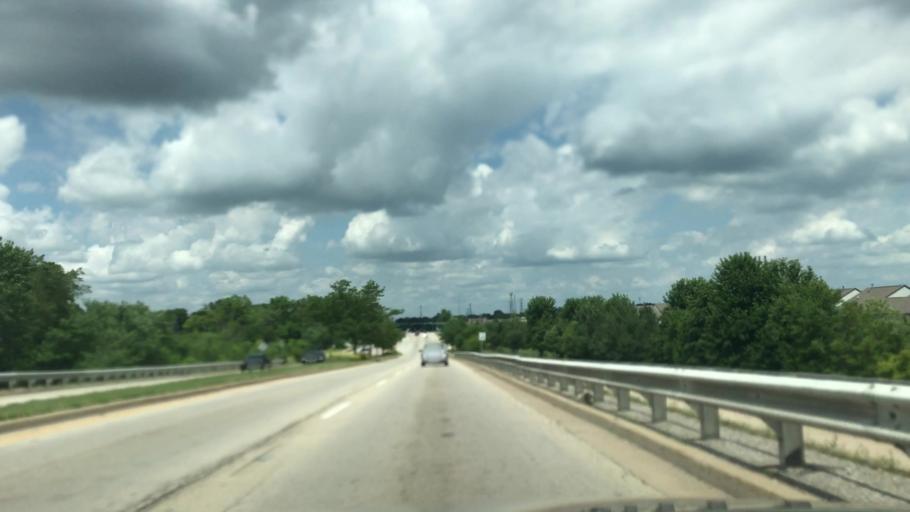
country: US
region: Illinois
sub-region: DuPage County
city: Warrenville
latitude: 41.7761
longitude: -88.2410
